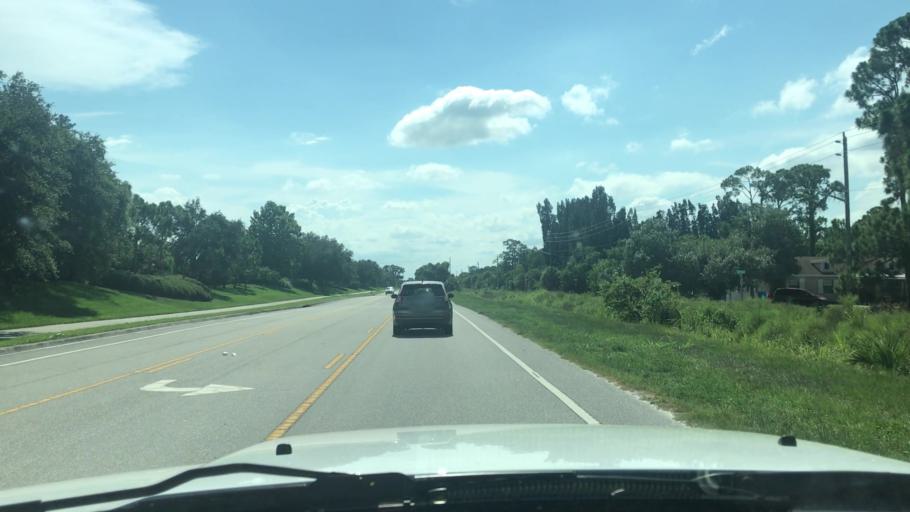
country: US
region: Florida
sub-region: Indian River County
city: Florida Ridge
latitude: 27.5722
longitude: -80.4073
